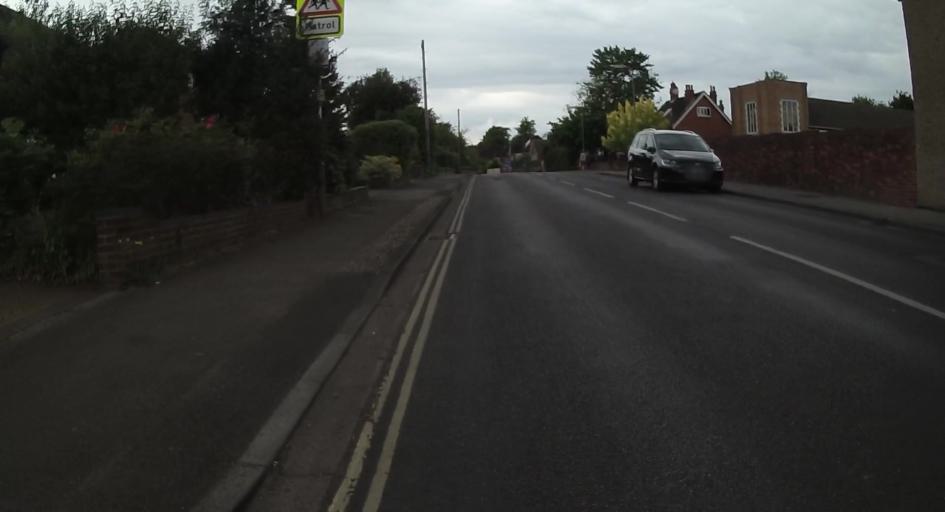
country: GB
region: England
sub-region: Hampshire
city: Aldershot
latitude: 51.2403
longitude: -0.7533
